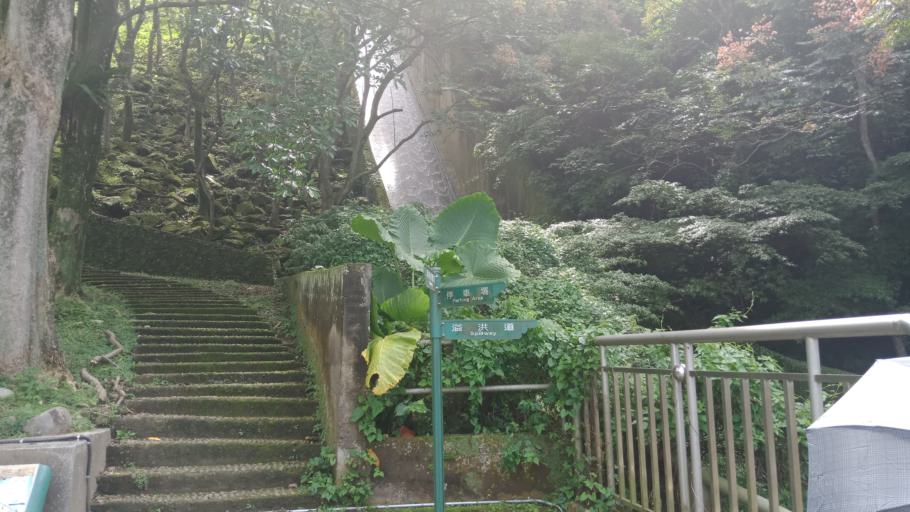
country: TW
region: Taiwan
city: Daxi
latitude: 24.8154
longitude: 121.2502
